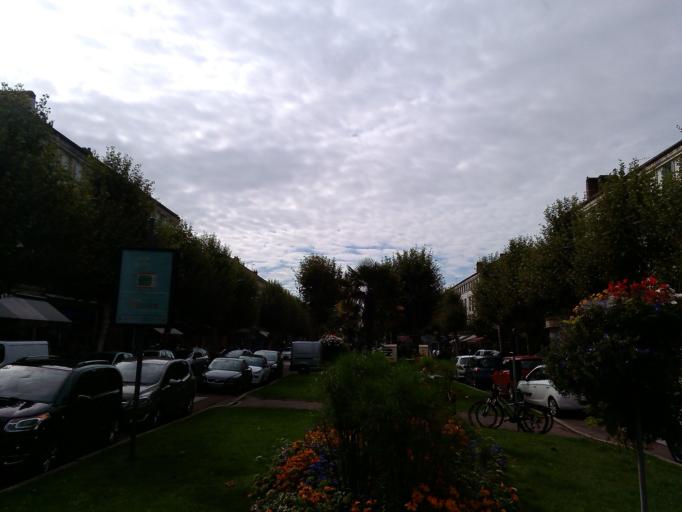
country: FR
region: Poitou-Charentes
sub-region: Departement de la Charente-Maritime
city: Royan
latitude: 45.6267
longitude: -1.0306
